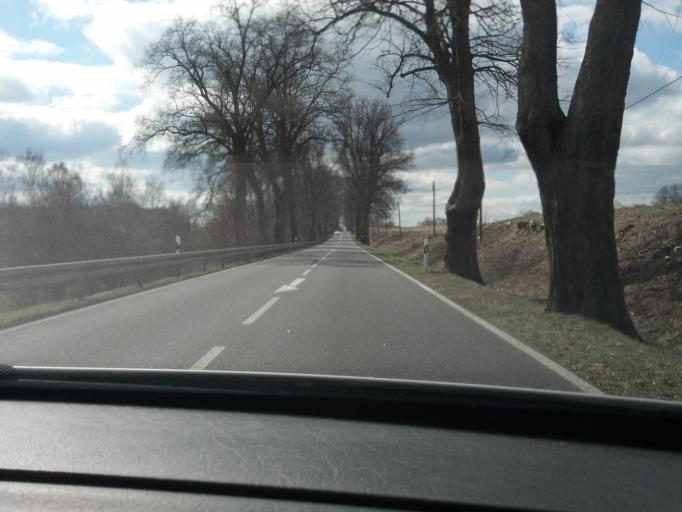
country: DE
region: Mecklenburg-Vorpommern
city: Blankensee
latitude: 53.3696
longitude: 13.2866
